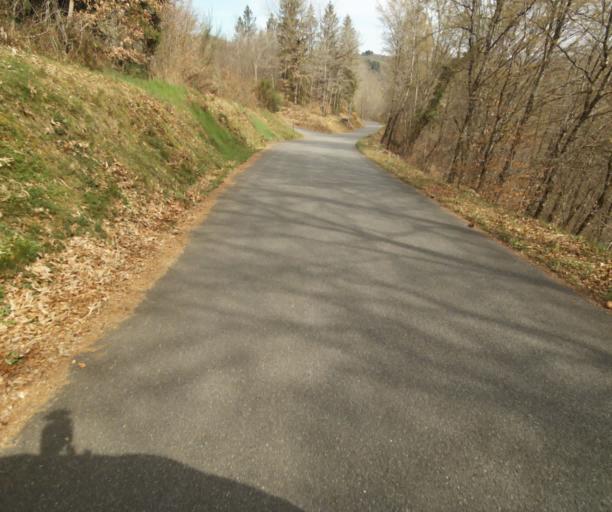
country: FR
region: Limousin
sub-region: Departement de la Correze
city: Naves
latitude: 45.3412
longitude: 1.8110
